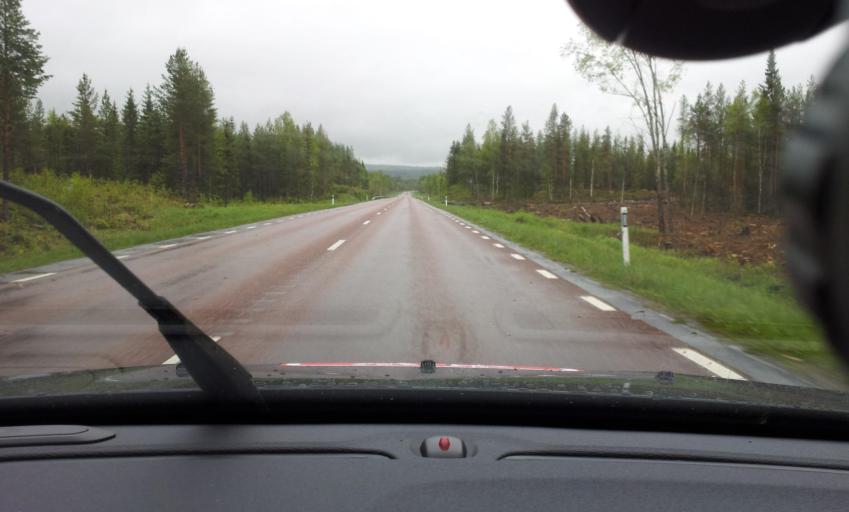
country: SE
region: Jaemtland
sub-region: Bergs Kommun
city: Hoverberg
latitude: 62.8198
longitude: 14.5165
